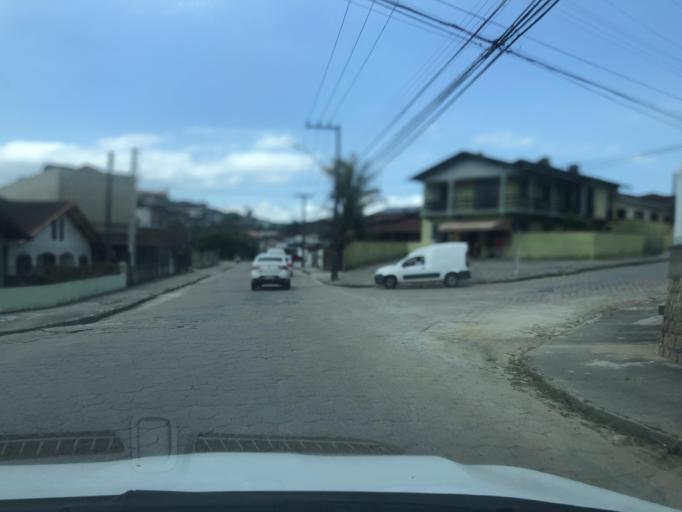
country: BR
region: Santa Catarina
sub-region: Joinville
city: Joinville
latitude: -26.3378
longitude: -48.8090
